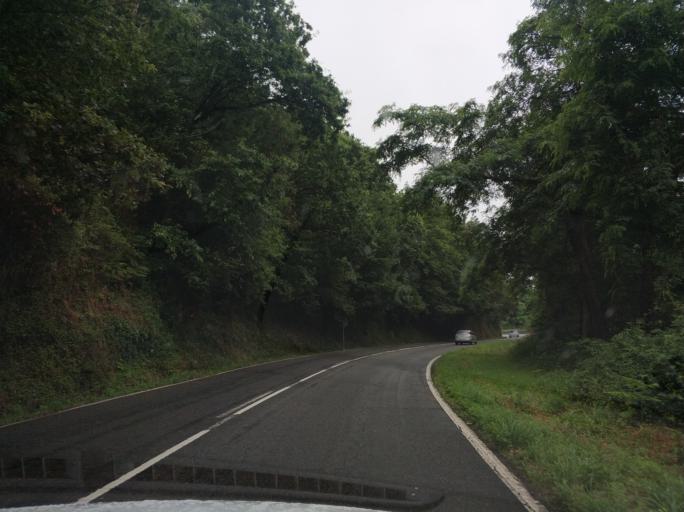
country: ES
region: Asturias
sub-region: Province of Asturias
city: Navia
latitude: 43.5357
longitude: -6.5310
